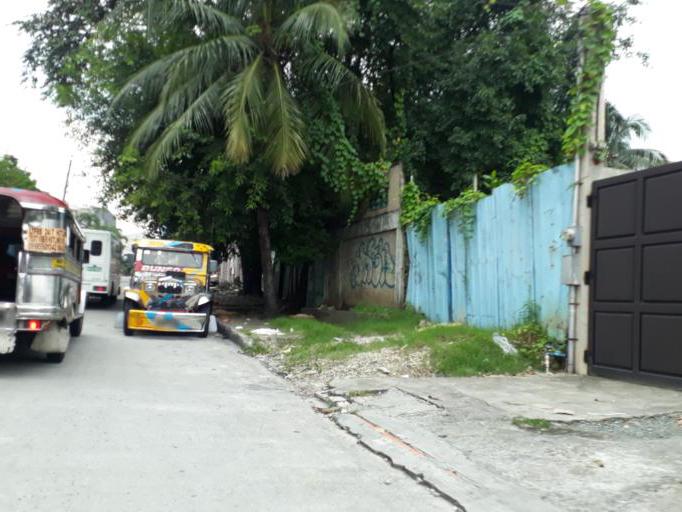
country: PH
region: Calabarzon
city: Bagong Pagasa
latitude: 14.6631
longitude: 121.0374
